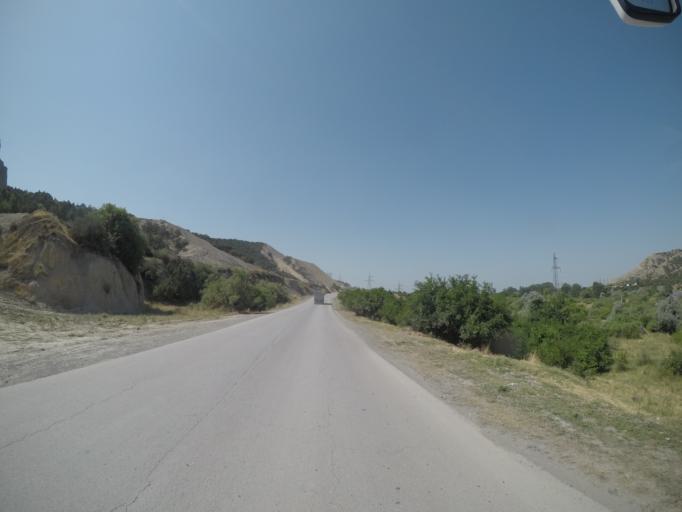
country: AZ
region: Agdas
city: Agdas
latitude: 40.7144
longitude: 47.5557
